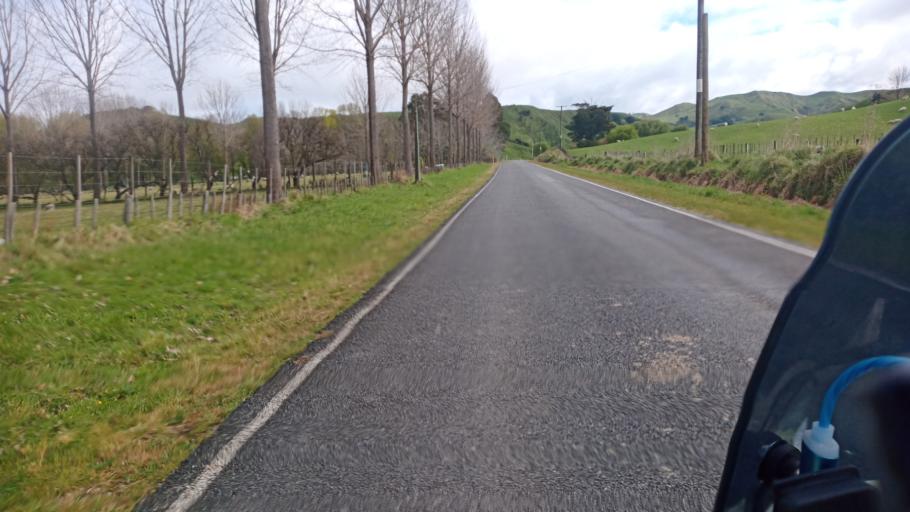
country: NZ
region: Gisborne
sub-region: Gisborne District
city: Gisborne
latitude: -38.5777
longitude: 178.1758
